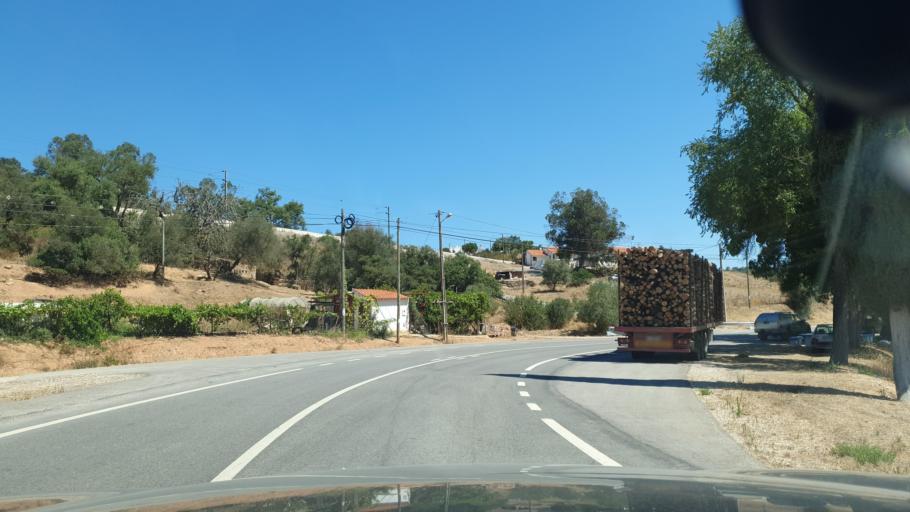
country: PT
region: Beja
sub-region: Odemira
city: Odemira
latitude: 37.5126
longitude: -8.4785
